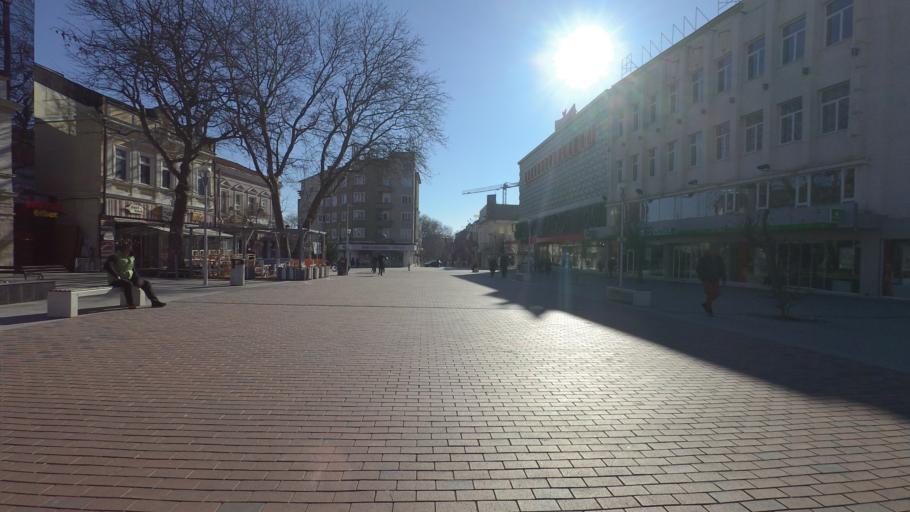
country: BG
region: Varna
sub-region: Obshtina Varna
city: Varna
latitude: 43.2034
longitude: 27.9129
